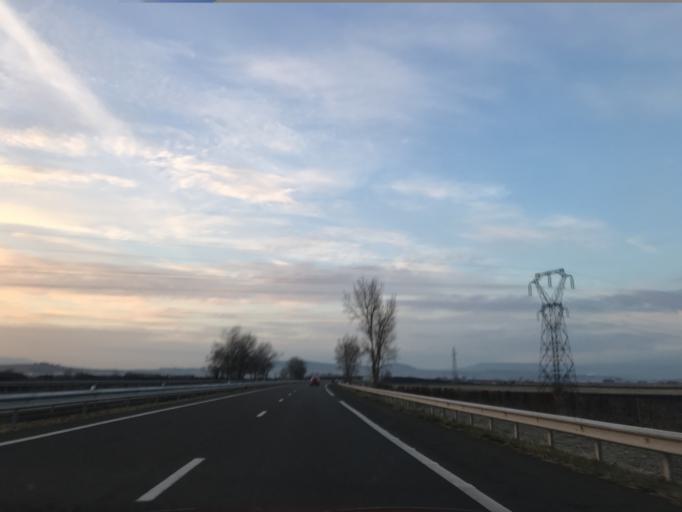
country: FR
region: Auvergne
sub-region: Departement du Puy-de-Dome
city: Pont-du-Chateau
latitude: 45.8108
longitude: 3.2214
